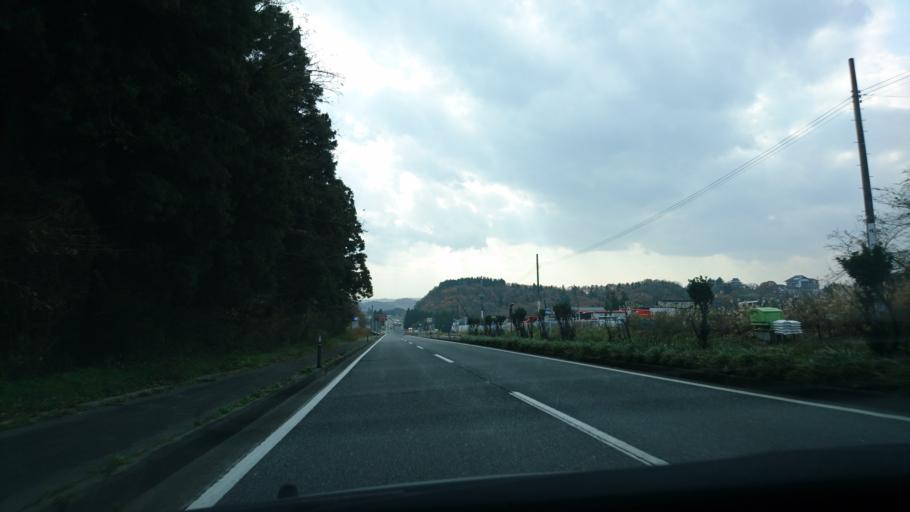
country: JP
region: Iwate
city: Ichinoseki
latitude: 39.0242
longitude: 141.1162
